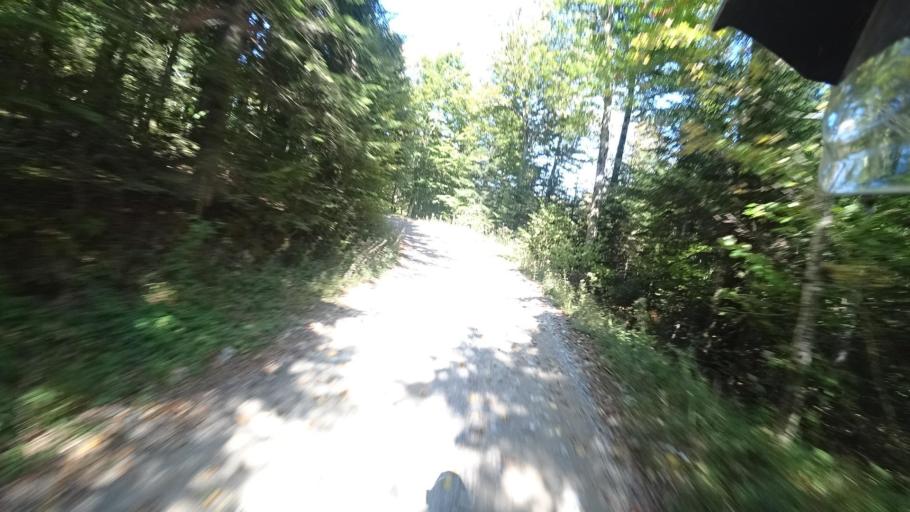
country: HR
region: Karlovacka
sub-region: Grad Ogulin
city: Ogulin
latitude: 45.2182
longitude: 15.1514
